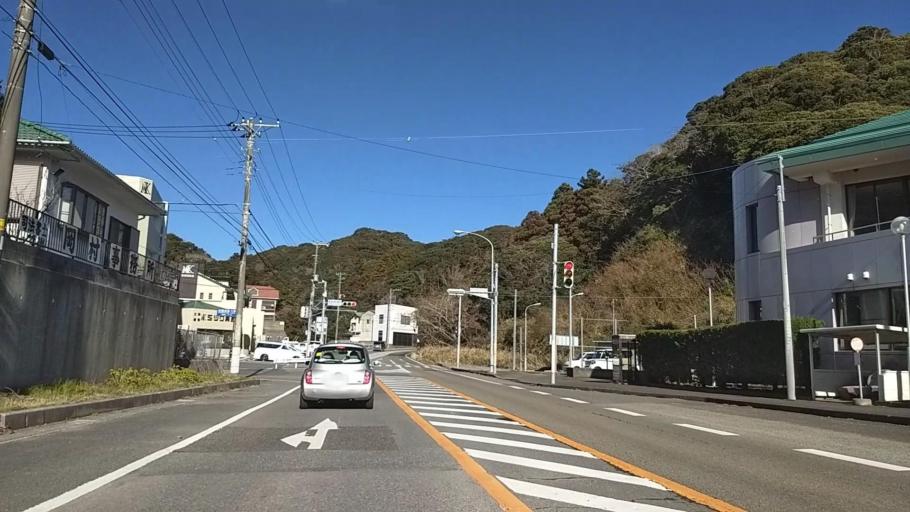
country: JP
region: Chiba
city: Katsuura
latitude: 35.1554
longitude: 140.3231
